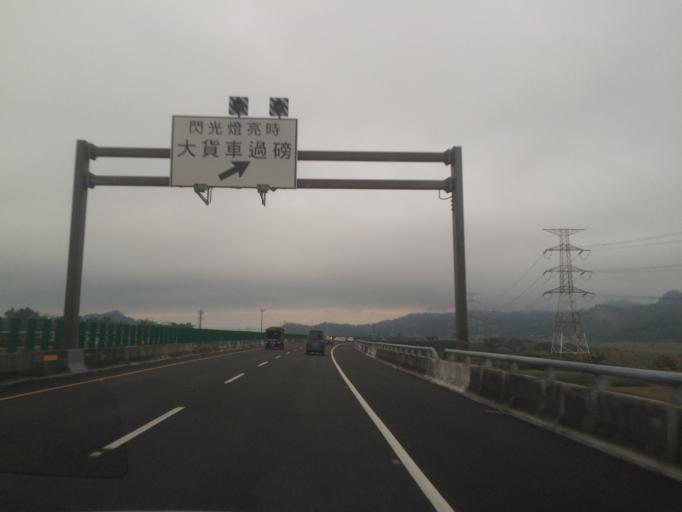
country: TW
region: Taiwan
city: Zhongxing New Village
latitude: 23.9967
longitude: 120.7446
